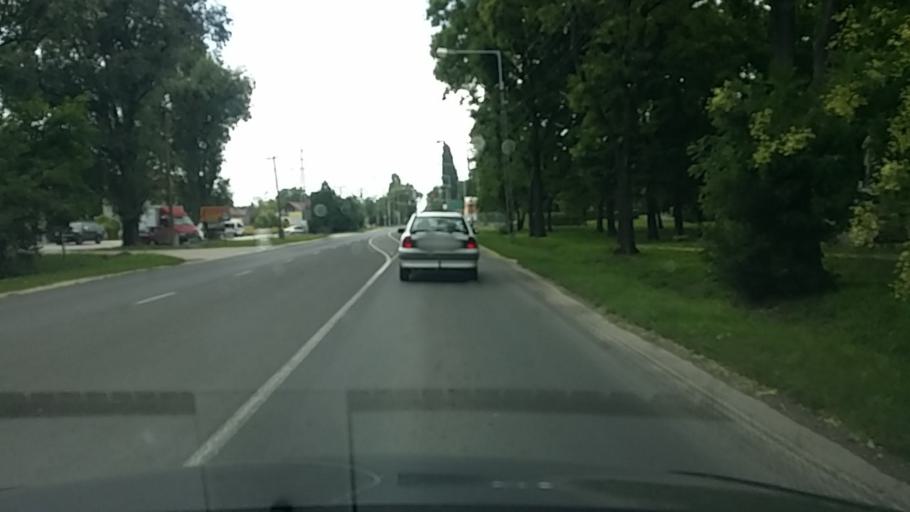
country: HU
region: Pest
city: Orkeny
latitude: 47.1263
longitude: 19.4303
